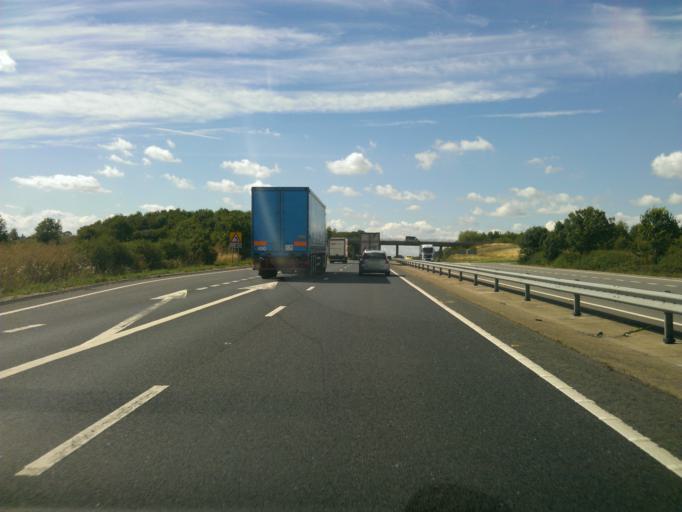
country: GB
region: England
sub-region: Bedford
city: Pertenhall
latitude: 52.3586
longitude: -0.4027
